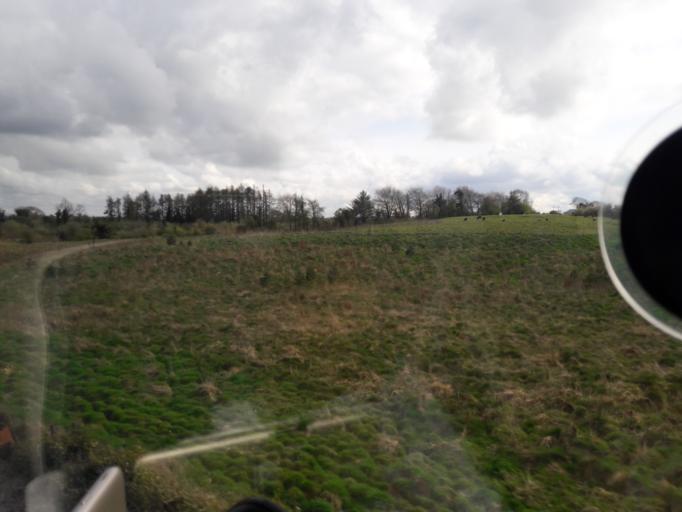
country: IE
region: Leinster
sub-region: An Iarmhi
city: An Muileann gCearr
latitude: 53.5032
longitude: -7.2738
